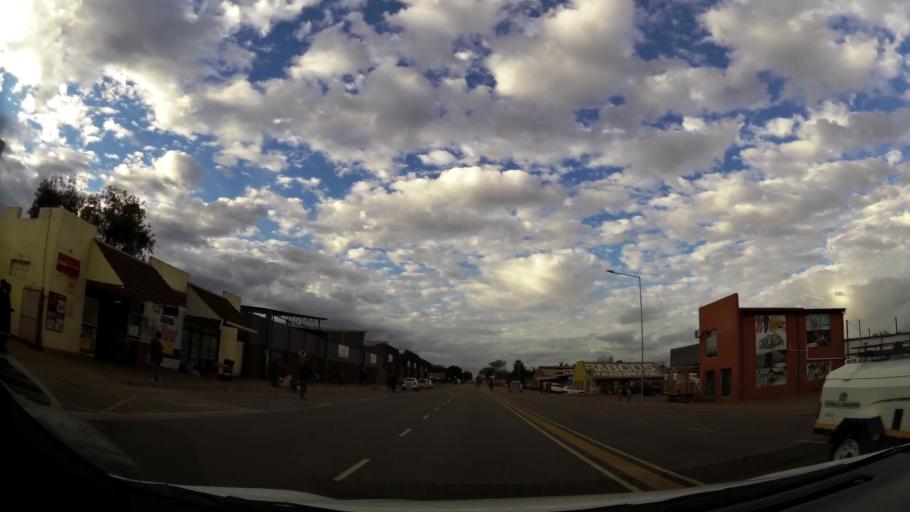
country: ZA
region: Limpopo
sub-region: Waterberg District Municipality
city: Modimolle
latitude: -24.5173
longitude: 28.7165
